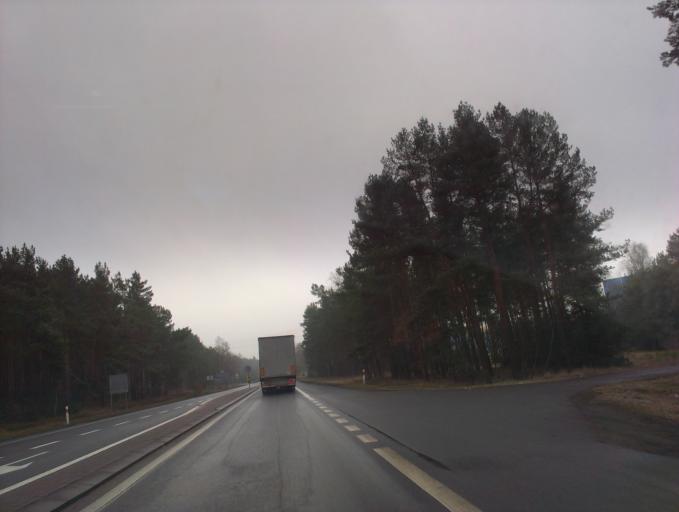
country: PL
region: Greater Poland Voivodeship
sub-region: Powiat pilski
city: Pila
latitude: 53.1716
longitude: 16.7792
